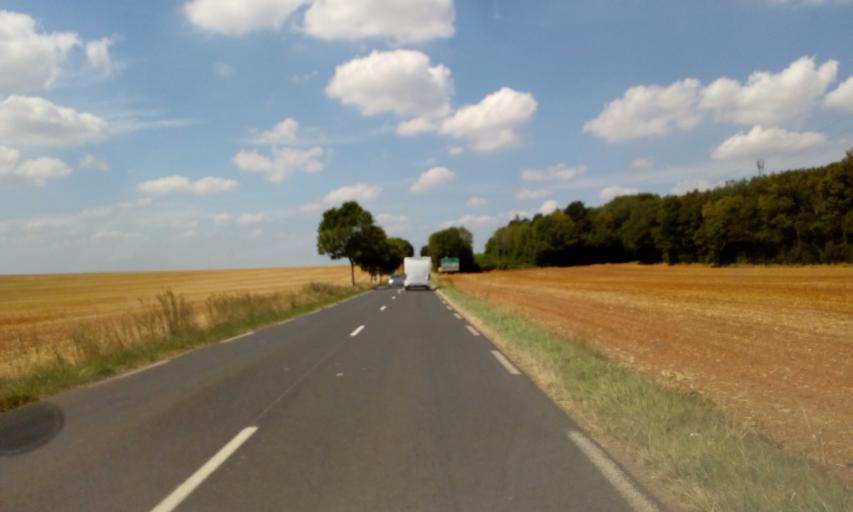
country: FR
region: Lorraine
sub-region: Departement de Meurthe-et-Moselle
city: Montauville
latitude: 48.8951
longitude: 5.9759
